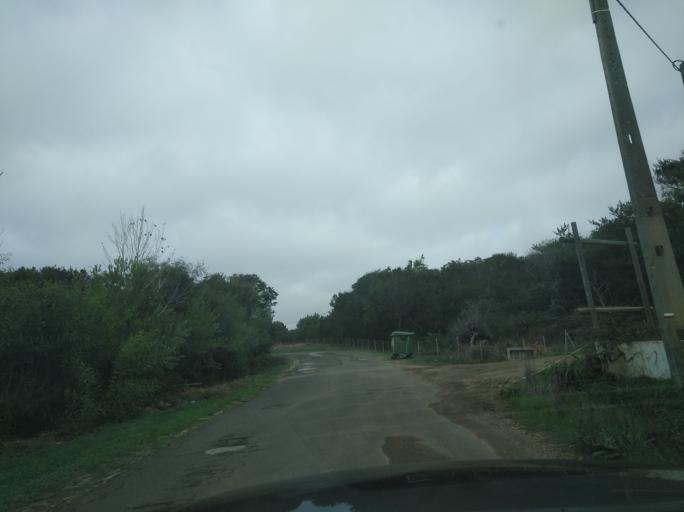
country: PT
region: Setubal
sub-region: Sines
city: Porto Covo
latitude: 37.8319
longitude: -8.7869
